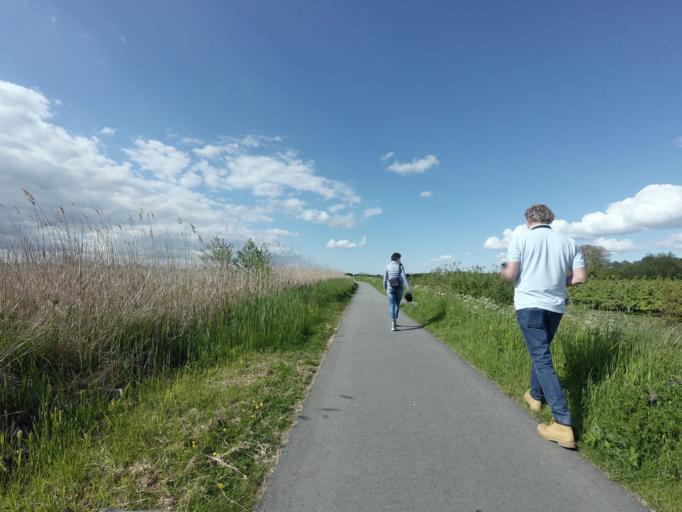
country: NL
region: Utrecht
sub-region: Gemeente Lopik
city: Lopik
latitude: 51.9543
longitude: 4.9913
